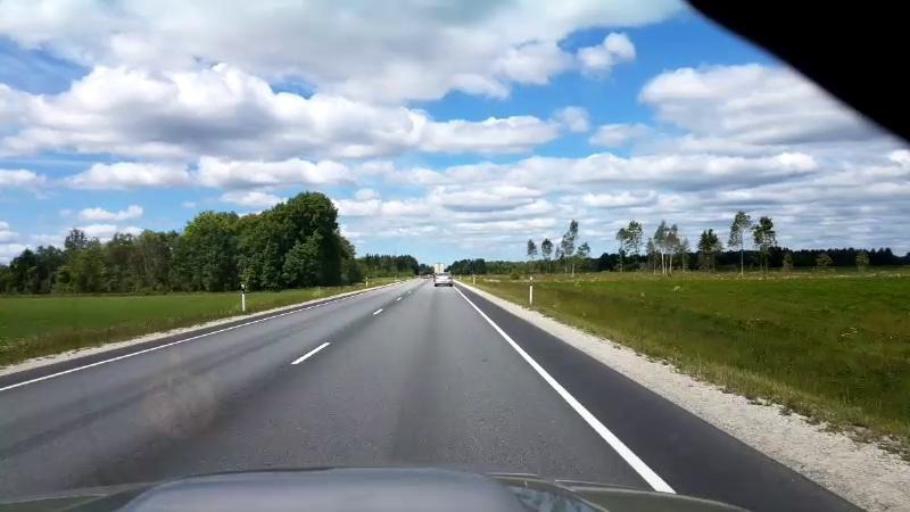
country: EE
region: Paernumaa
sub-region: Halinga vald
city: Parnu-Jaagupi
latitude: 58.6443
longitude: 24.4869
